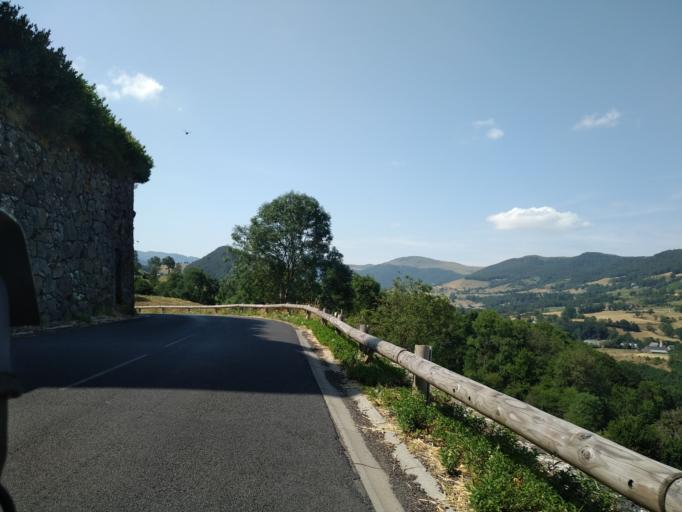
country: FR
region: Auvergne
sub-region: Departement du Cantal
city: Riom-es-Montagnes
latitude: 45.1985
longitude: 2.7173
